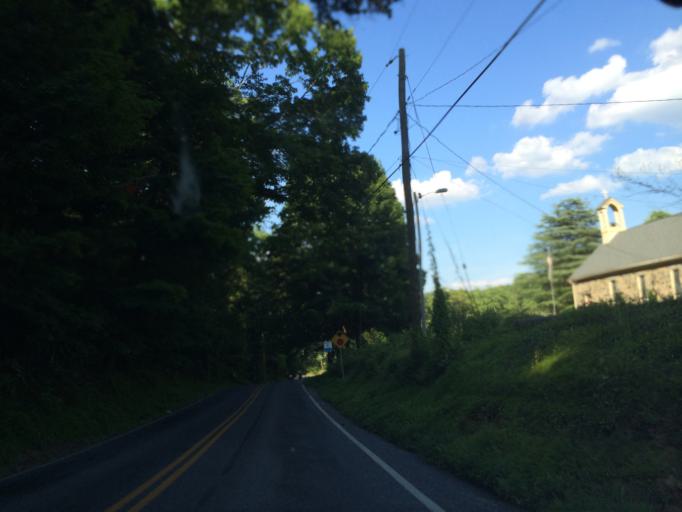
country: US
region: Maryland
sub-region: Carroll County
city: Sykesville
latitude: 39.3610
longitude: -76.9707
